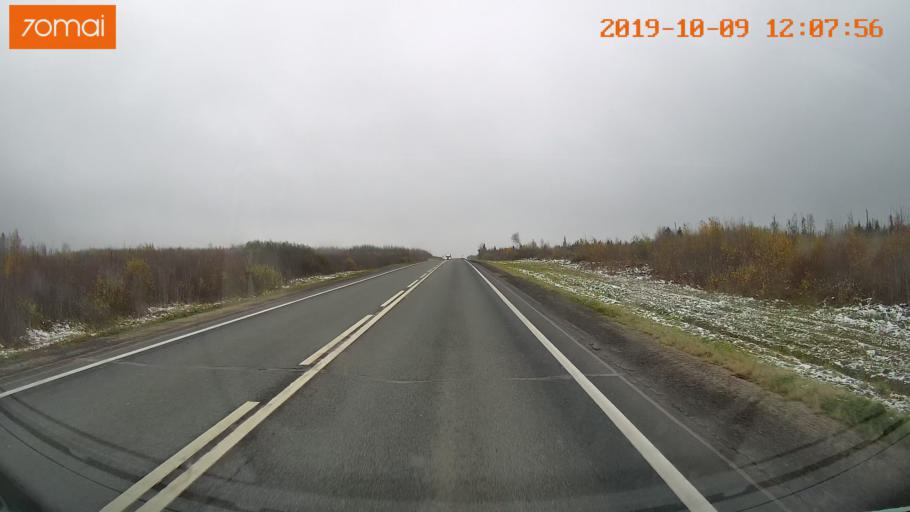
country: RU
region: Jaroslavl
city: Prechistoye
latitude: 58.5931
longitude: 40.3448
